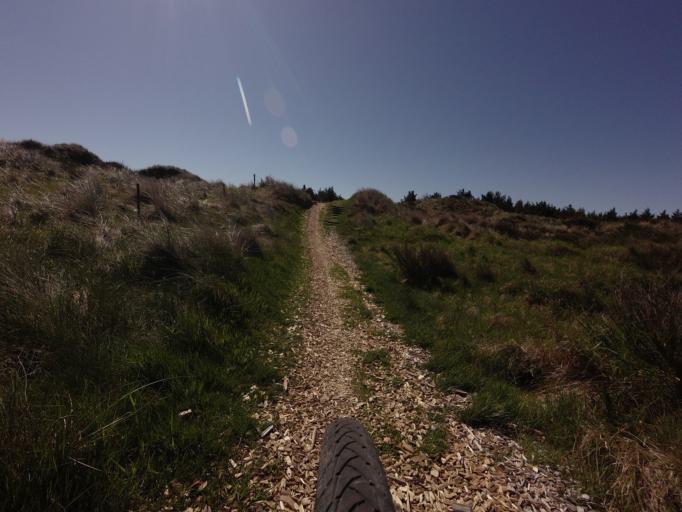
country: DK
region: North Denmark
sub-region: Jammerbugt Kommune
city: Pandrup
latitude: 57.2987
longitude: 9.6439
